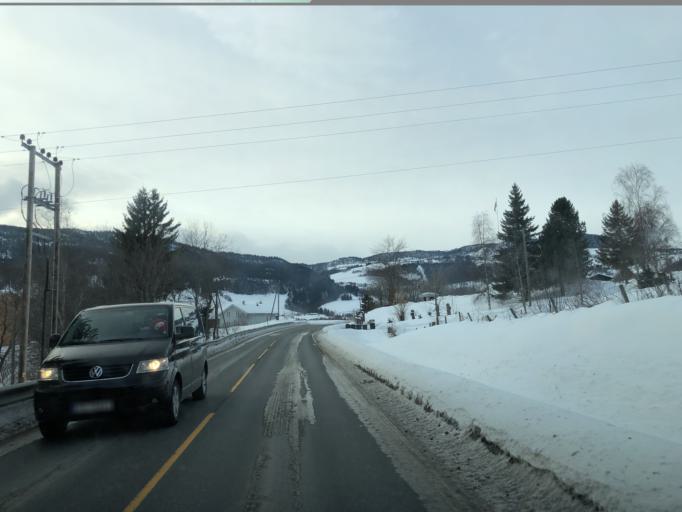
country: NO
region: Oppland
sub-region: Gausdal
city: Segalstad bru
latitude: 61.2610
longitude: 10.1614
